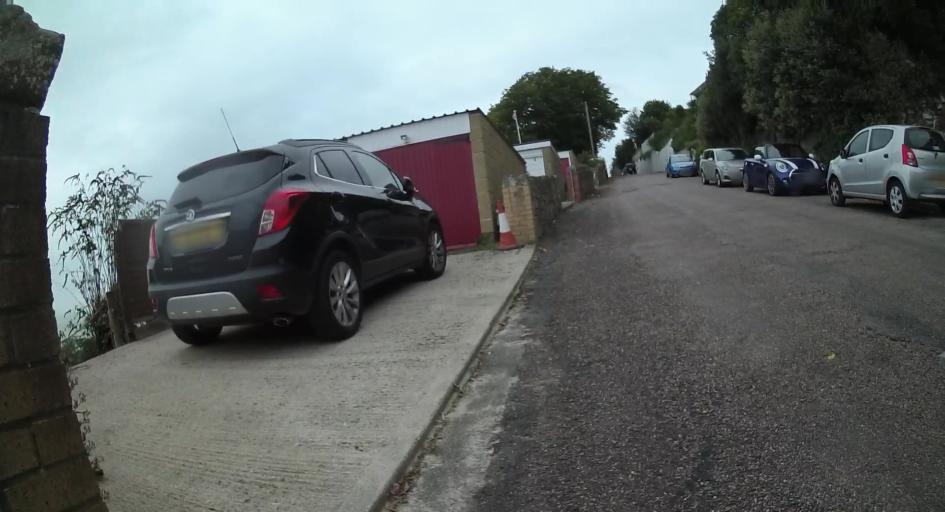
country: GB
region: England
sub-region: Isle of Wight
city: Ventnor
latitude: 50.5957
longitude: -1.2116
